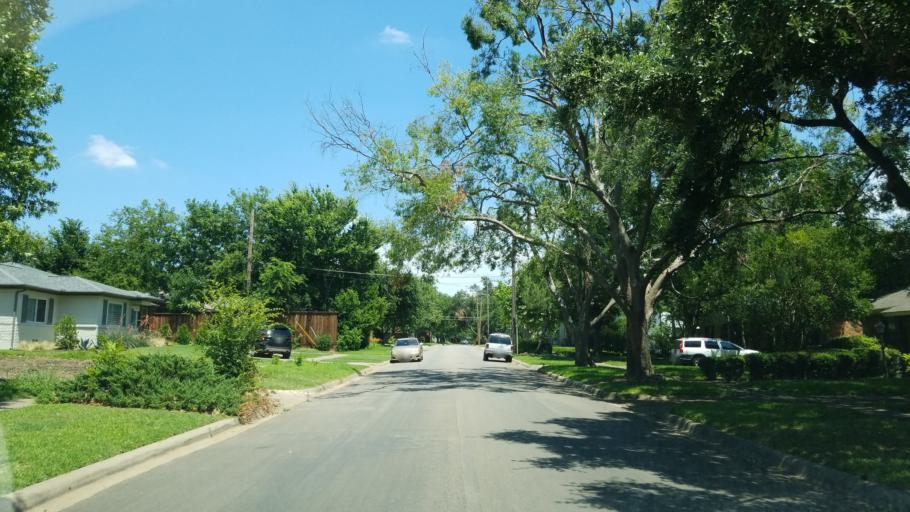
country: US
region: Texas
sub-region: Dallas County
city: University Park
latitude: 32.8753
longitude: -96.8438
